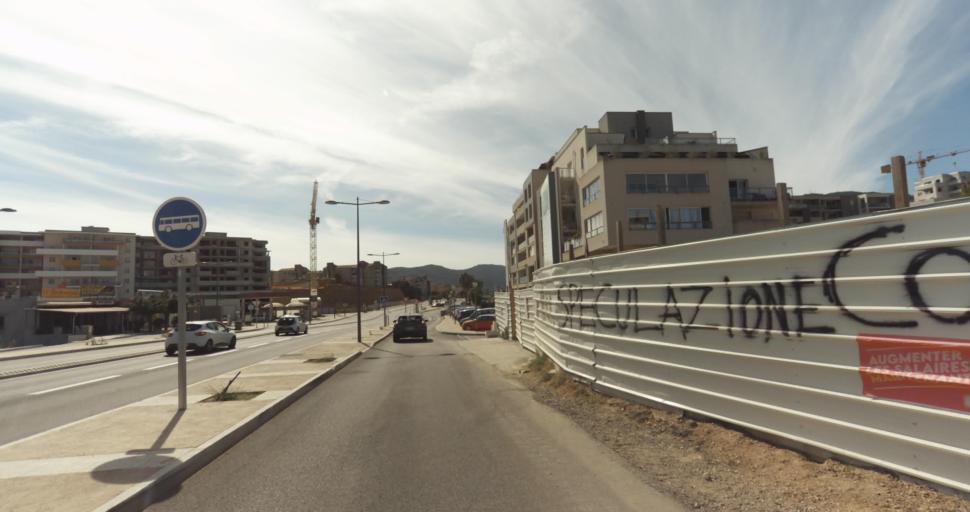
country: FR
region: Corsica
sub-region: Departement de la Corse-du-Sud
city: Ajaccio
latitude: 41.9434
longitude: 8.7533
